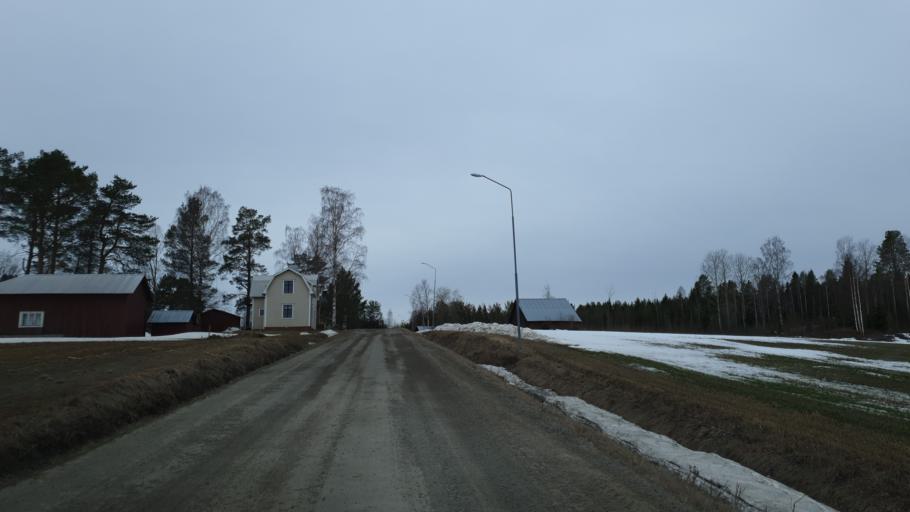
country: SE
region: Vaesterbotten
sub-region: Robertsfors Kommun
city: Robertsfors
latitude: 64.3778
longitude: 20.9065
